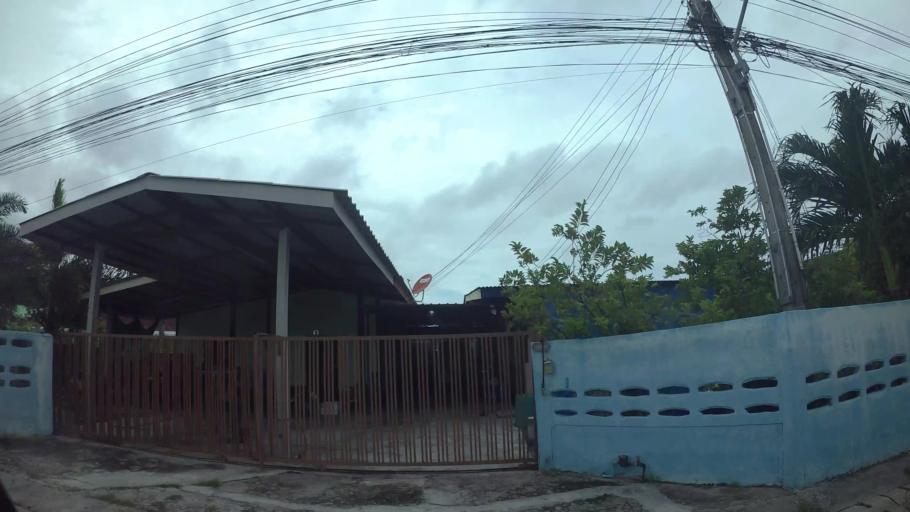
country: TH
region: Rayong
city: Rayong
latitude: 12.6639
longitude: 101.2695
